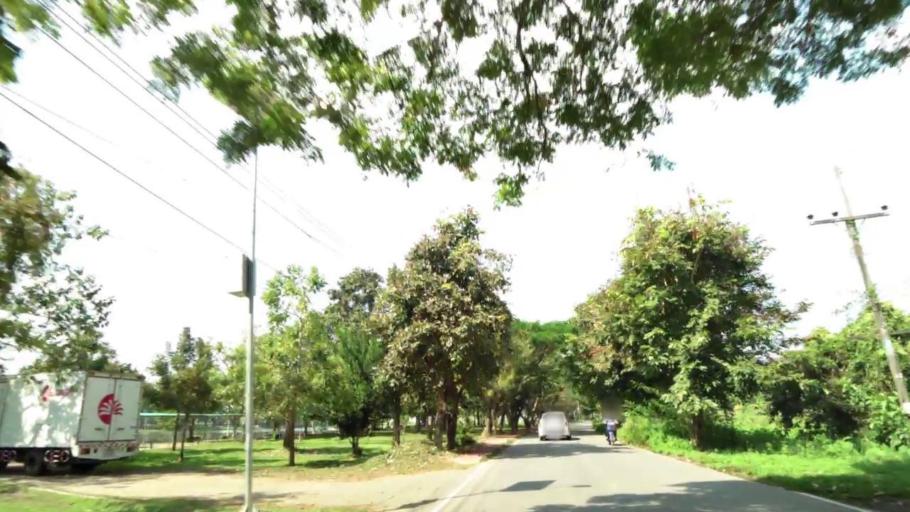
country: TH
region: Chiang Rai
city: Chiang Rai
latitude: 19.8865
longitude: 99.8050
